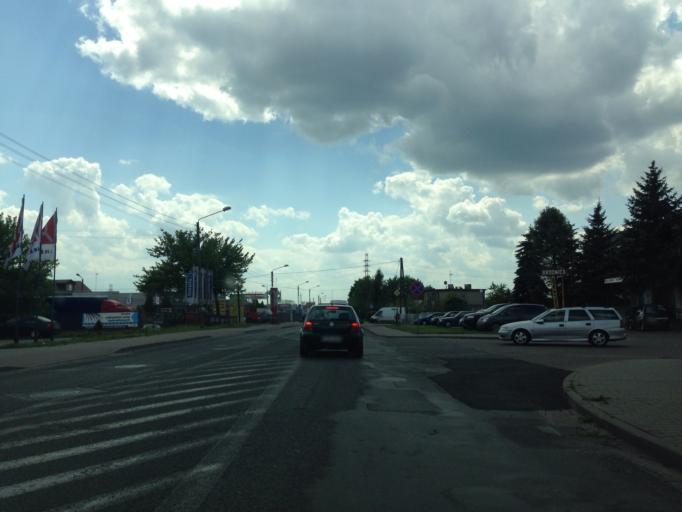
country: PL
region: Kujawsko-Pomorskie
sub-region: Powiat brodnicki
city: Brodnica
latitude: 53.2404
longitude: 19.3938
